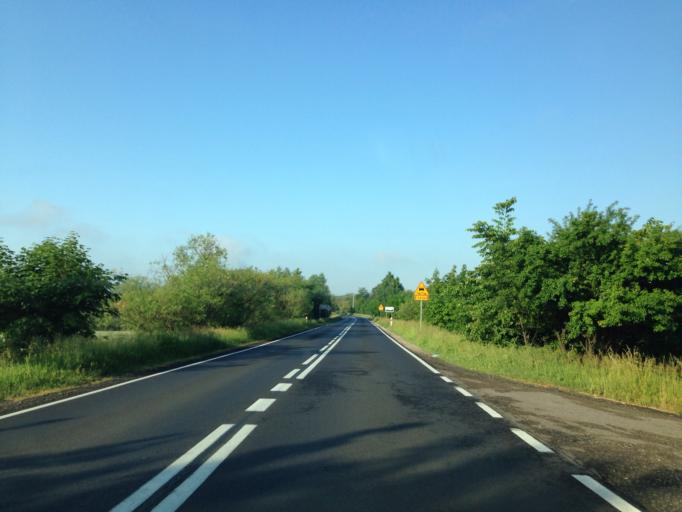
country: PL
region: Kujawsko-Pomorskie
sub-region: Grudziadz
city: Grudziadz
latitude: 53.5270
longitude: 18.8137
